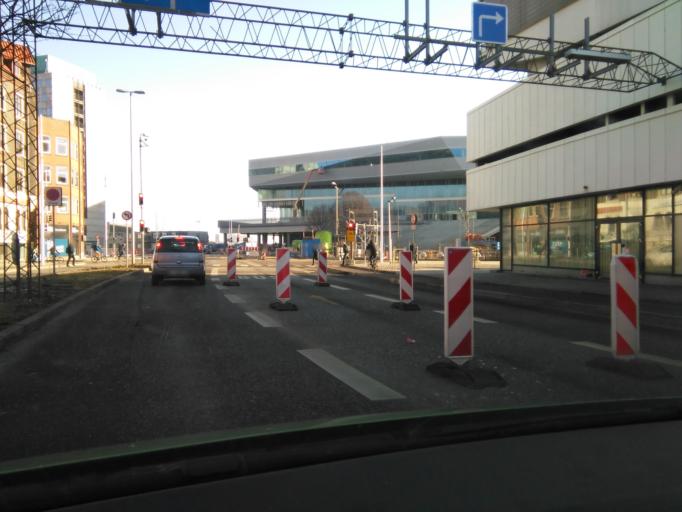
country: DK
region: Central Jutland
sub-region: Arhus Kommune
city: Arhus
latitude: 56.1528
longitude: 10.2117
